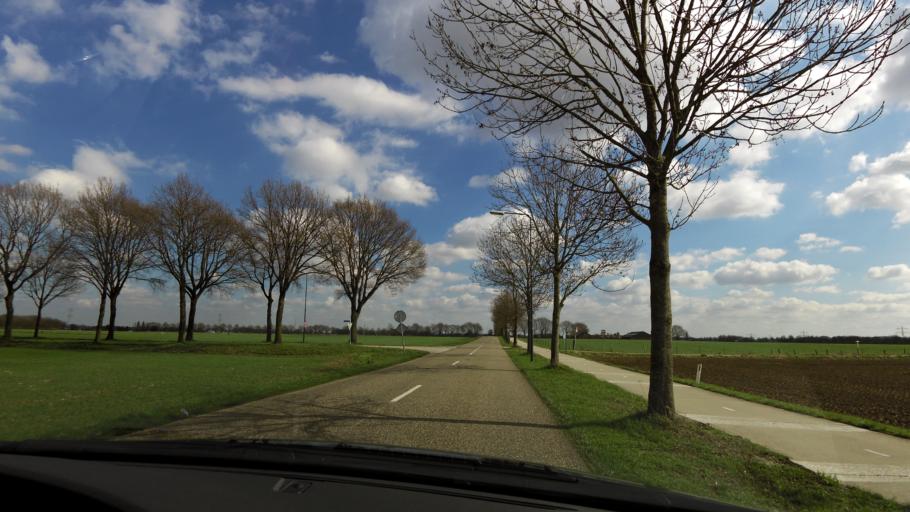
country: NL
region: Limburg
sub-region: Gemeente Sittard-Geleen
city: Limbricht
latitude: 50.9970
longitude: 5.8080
